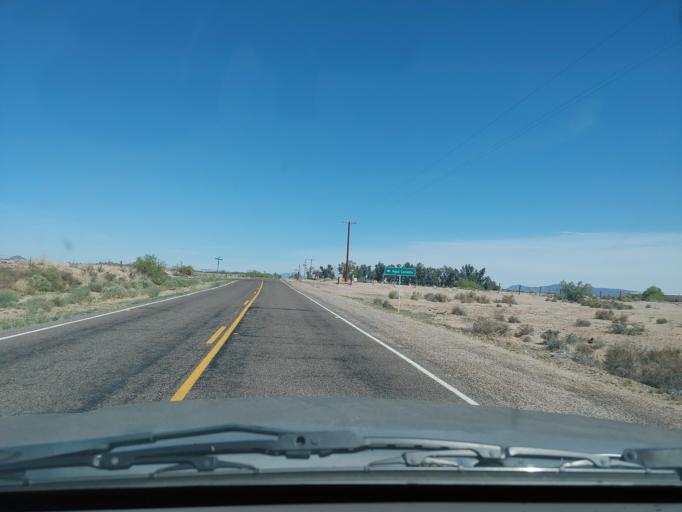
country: US
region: Arizona
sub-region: Maricopa County
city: Gila Bend
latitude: 32.9856
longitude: -113.3060
